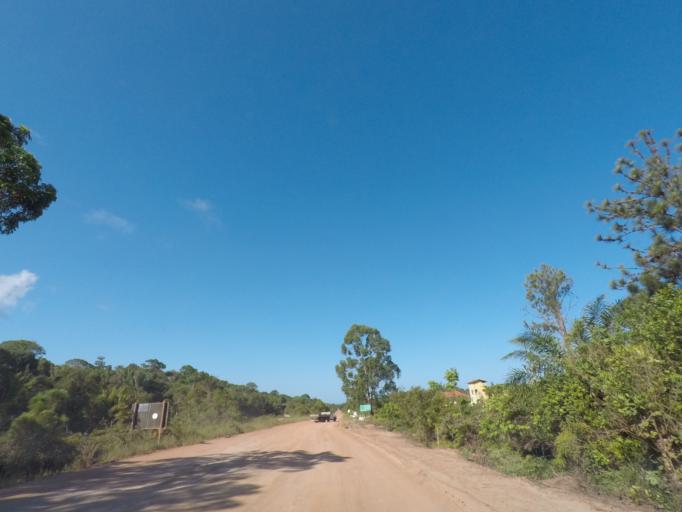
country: BR
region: Bahia
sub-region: Marau
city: Marau
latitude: -14.1093
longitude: -38.9826
